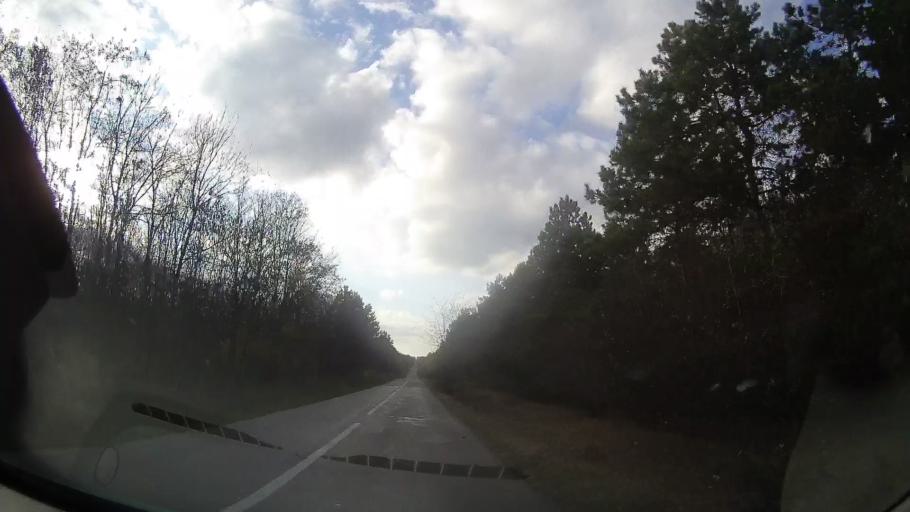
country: RO
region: Constanta
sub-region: Comuna Negru Voda
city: Negru Voda
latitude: 43.8193
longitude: 28.2713
